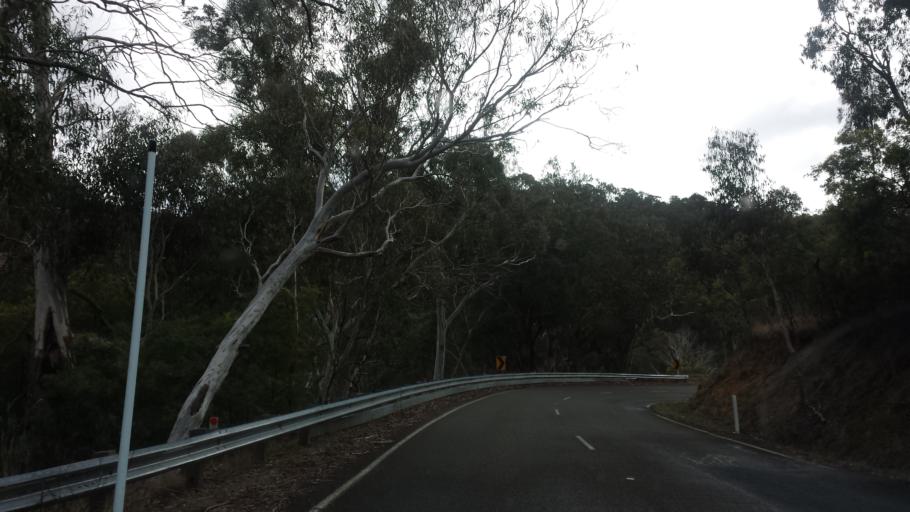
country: AU
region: Victoria
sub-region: Alpine
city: Mount Beauty
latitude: -37.1162
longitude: 147.5578
